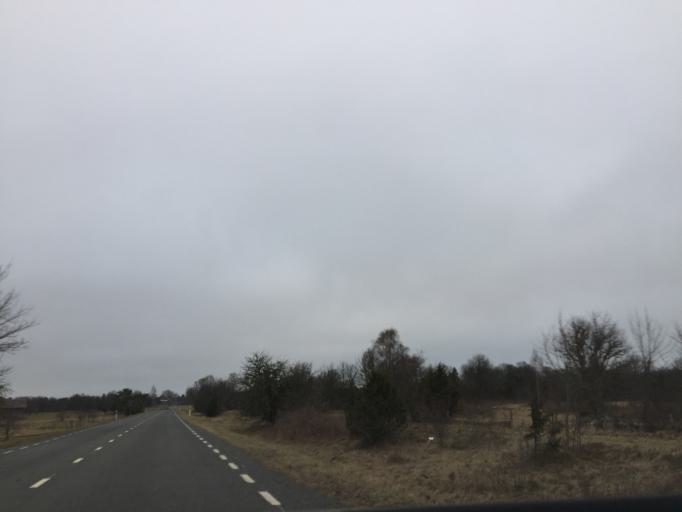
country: EE
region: Saare
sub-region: Kuressaare linn
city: Kuressaare
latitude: 58.5341
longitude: 22.3401
